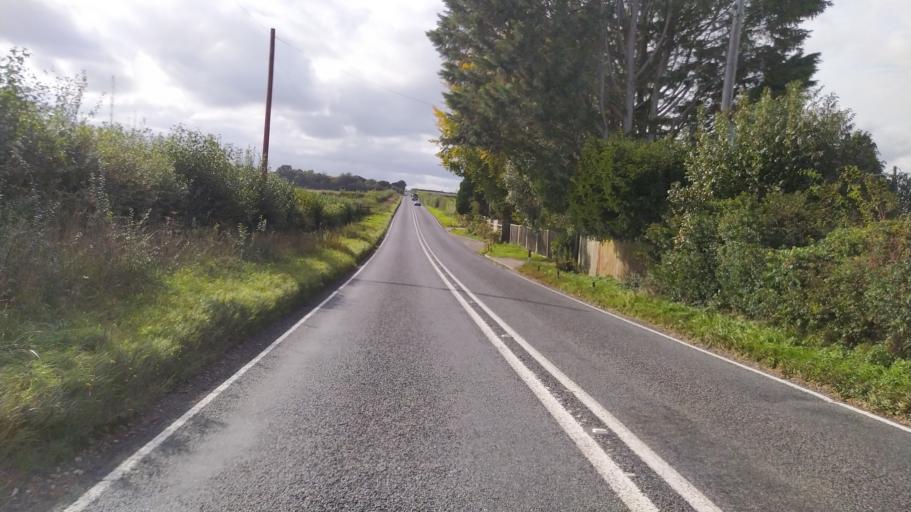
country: GB
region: England
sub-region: Hampshire
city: Winchester
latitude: 51.1365
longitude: -1.3969
